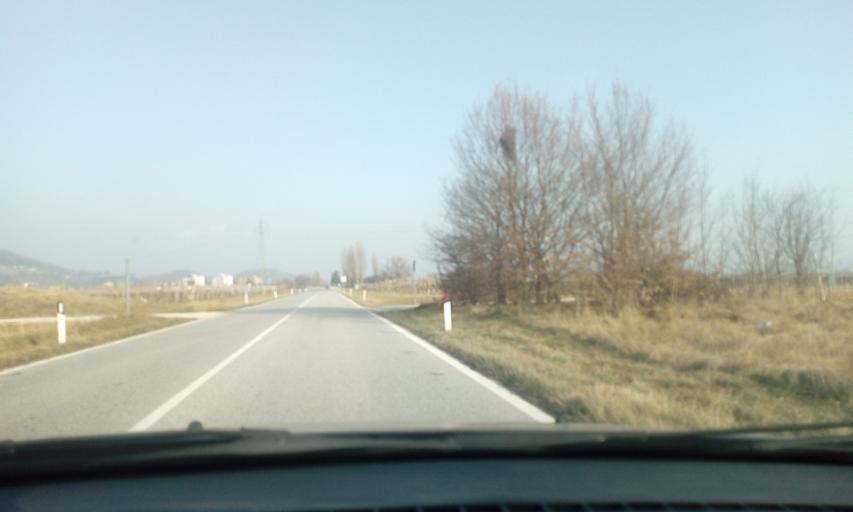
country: IT
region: Friuli Venezia Giulia
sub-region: Provincia di Gorizia
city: Cormons
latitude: 45.9527
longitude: 13.4460
